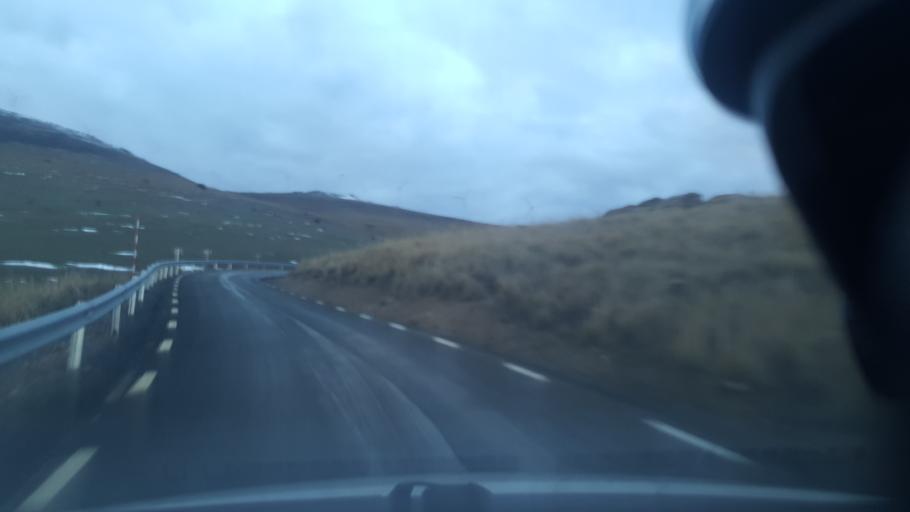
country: ES
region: Castille and Leon
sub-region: Provincia de Avila
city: Ojos-Albos
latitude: 40.7048
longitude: -4.4463
